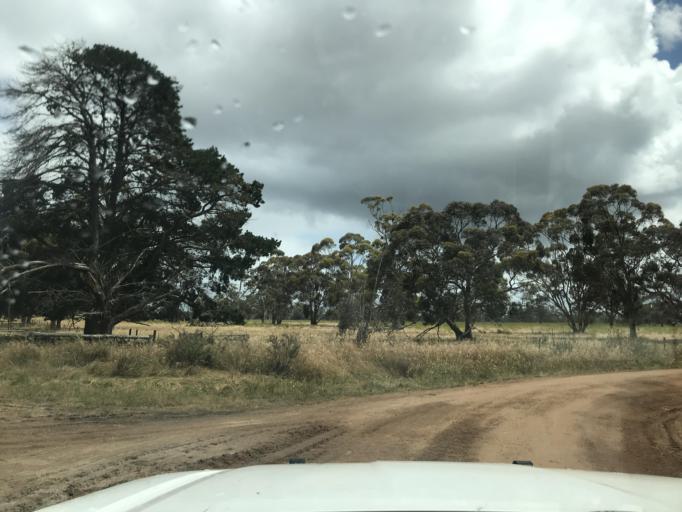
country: AU
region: South Australia
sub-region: Wattle Range
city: Penola
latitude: -37.1267
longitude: 141.3154
